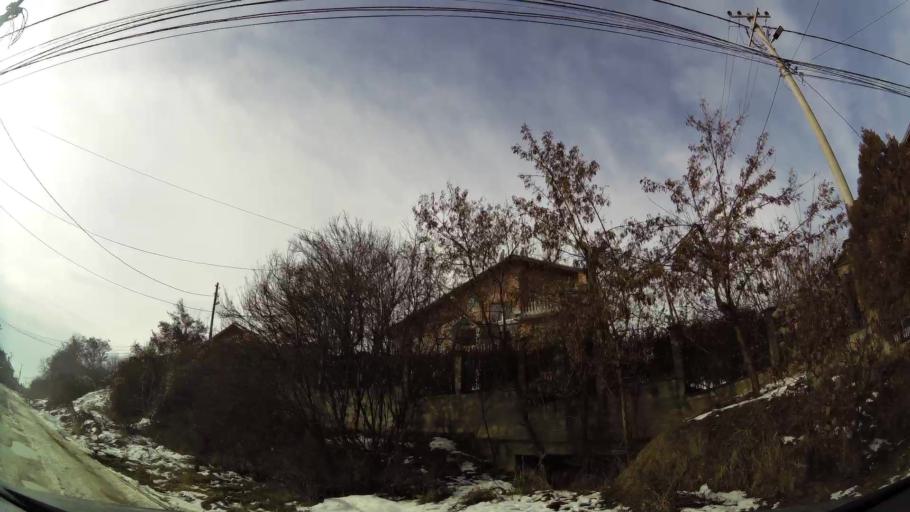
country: XK
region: Pristina
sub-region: Komuna e Prishtines
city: Pristina
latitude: 42.6834
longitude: 21.1739
